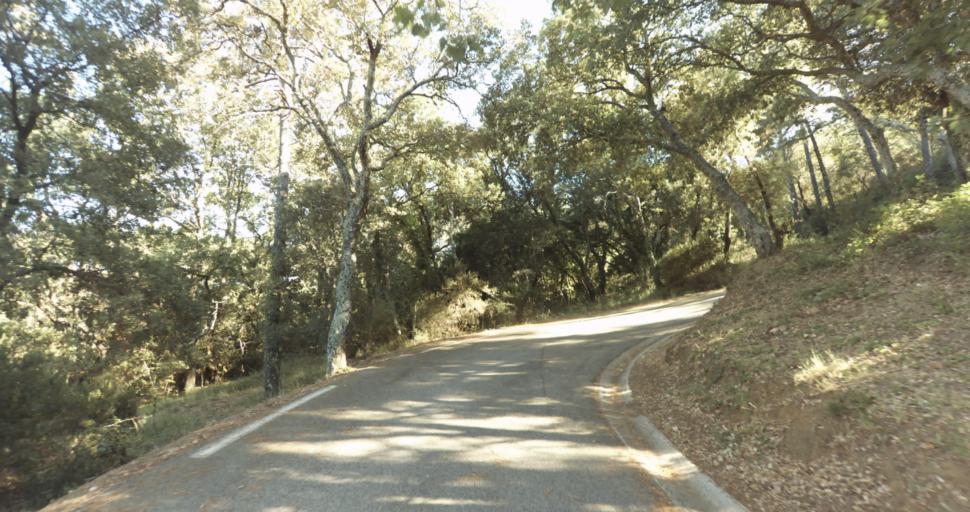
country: FR
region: Provence-Alpes-Cote d'Azur
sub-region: Departement du Var
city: Gassin
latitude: 43.2307
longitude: 6.5883
